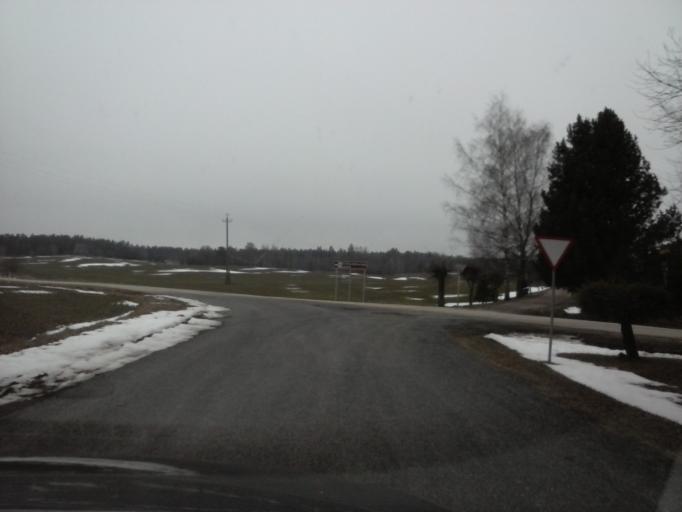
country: EE
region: Vorumaa
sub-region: Antsla vald
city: Vana-Antsla
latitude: 57.6081
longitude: 26.3499
